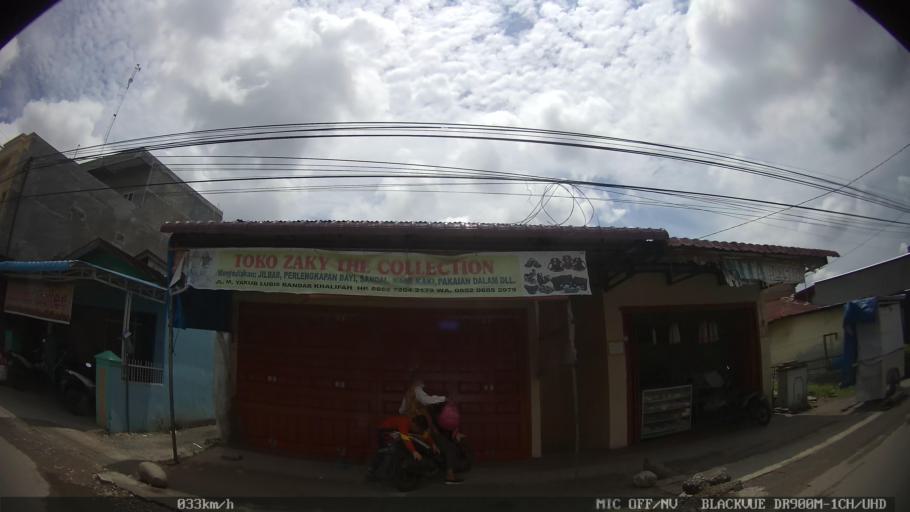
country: ID
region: North Sumatra
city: Medan
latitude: 3.6146
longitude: 98.7481
